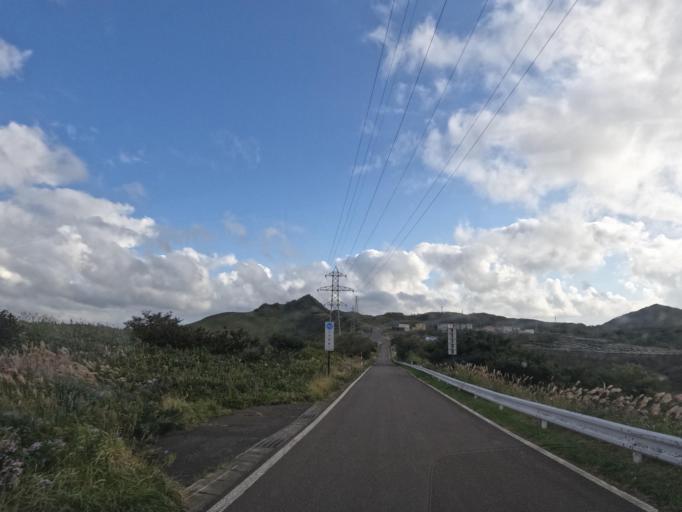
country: JP
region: Hokkaido
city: Muroran
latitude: 42.3129
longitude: 141.0060
